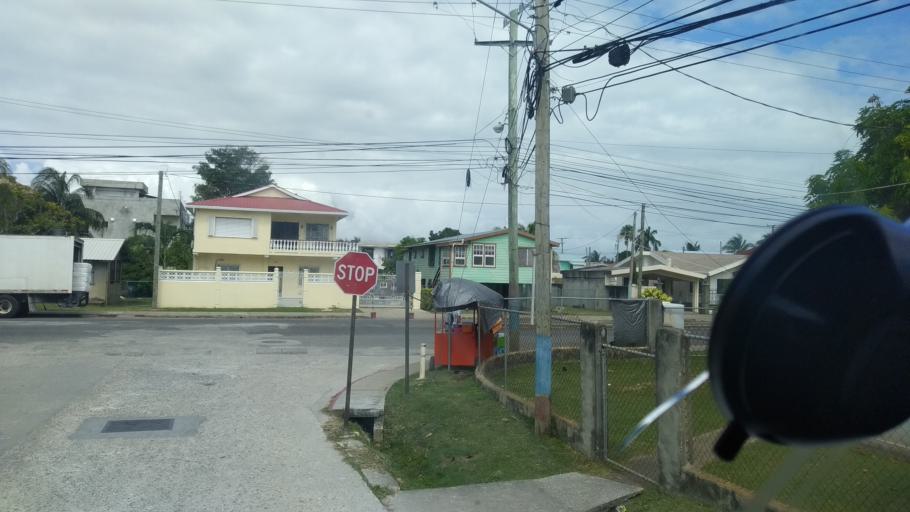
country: BZ
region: Belize
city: Belize City
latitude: 17.5085
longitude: -88.1936
